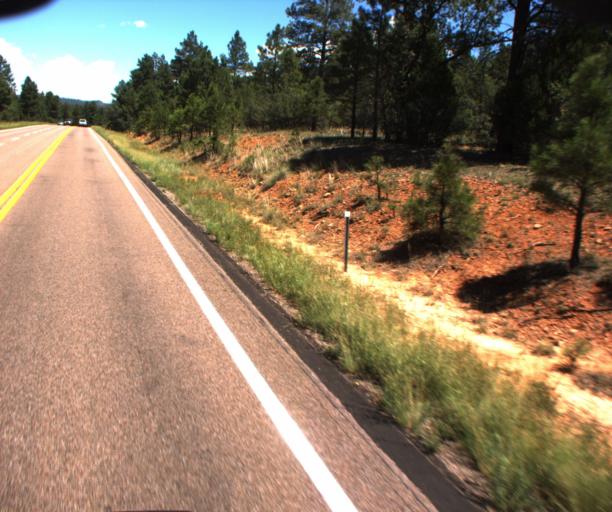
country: US
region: Arizona
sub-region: Navajo County
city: Linden
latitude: 34.0963
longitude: -110.1701
